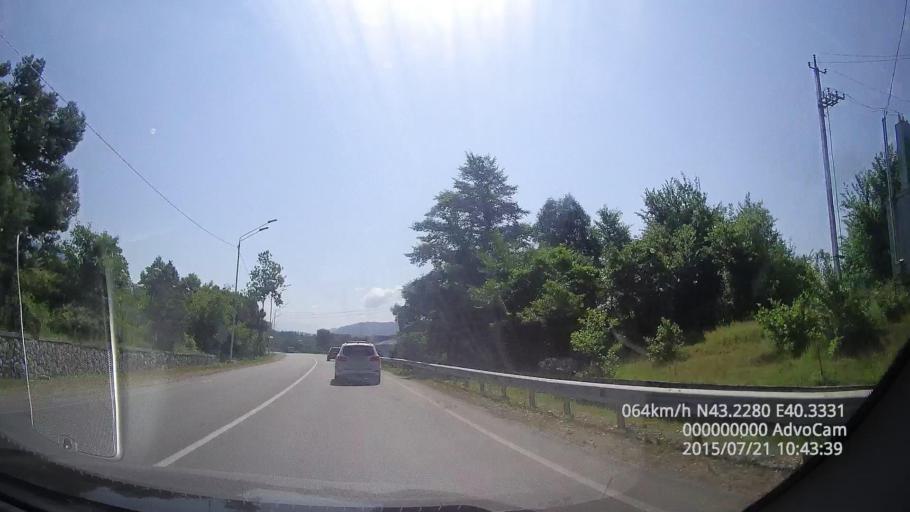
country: GE
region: Abkhazia
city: Bich'vinta
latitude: 43.2280
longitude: 40.3333
